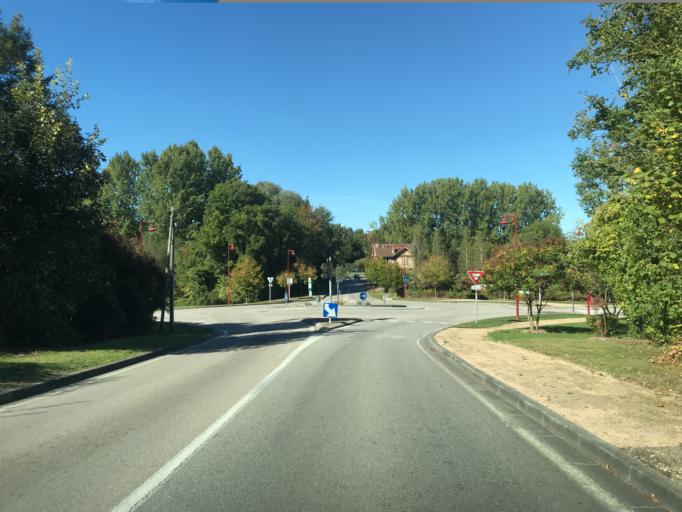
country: FR
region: Haute-Normandie
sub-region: Departement de l'Eure
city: Le Vaudreuil
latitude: 49.2466
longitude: 1.2101
